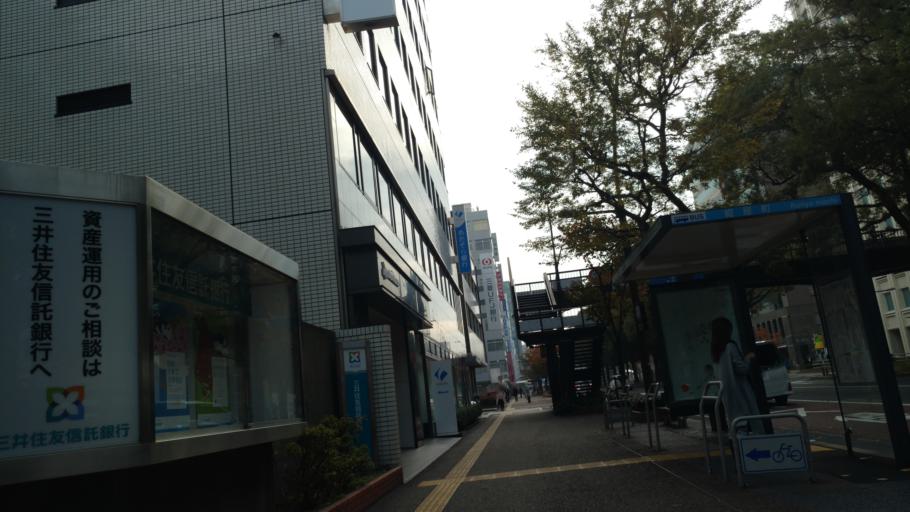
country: JP
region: Kagawa
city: Takamatsu-shi
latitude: 34.3443
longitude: 134.0483
